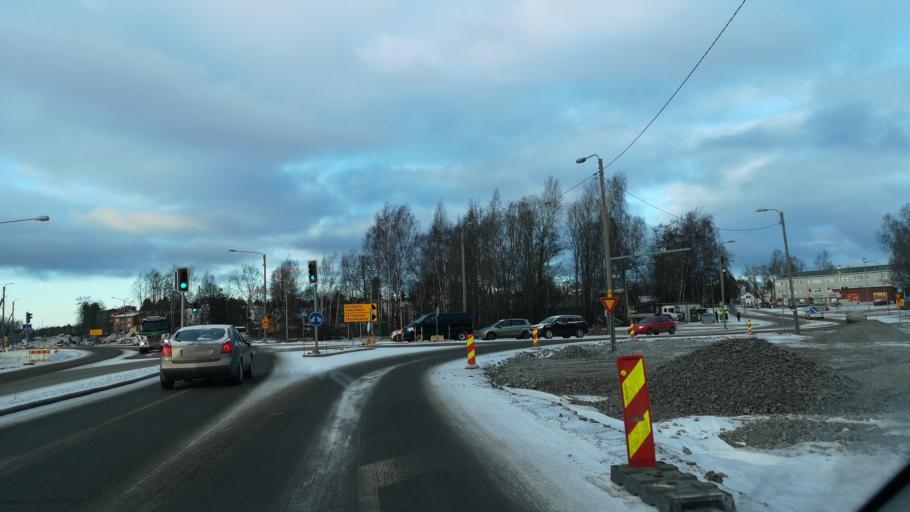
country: FI
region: Ostrobothnia
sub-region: Vaasa
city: Vaasa
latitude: 63.1133
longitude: 21.6182
